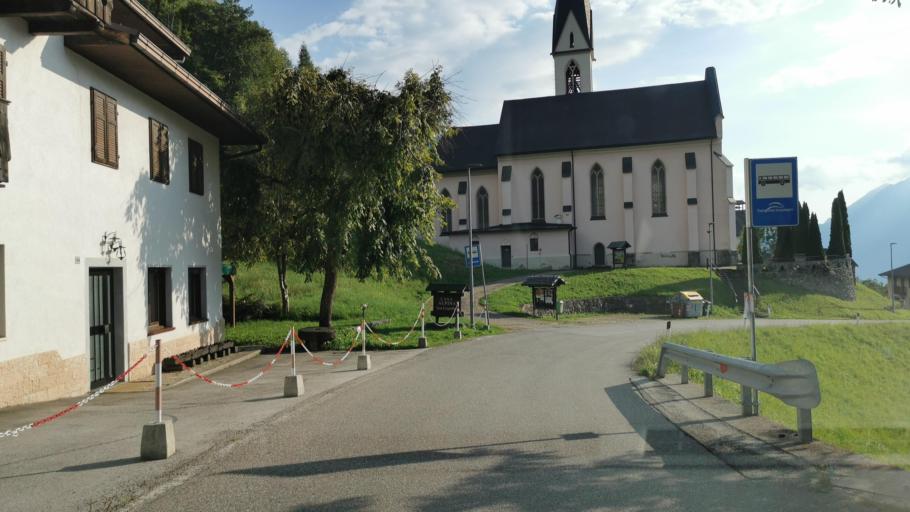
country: IT
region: Trentino-Alto Adige
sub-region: Provincia di Trento
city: Frassilongo
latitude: 46.0898
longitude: 11.2978
